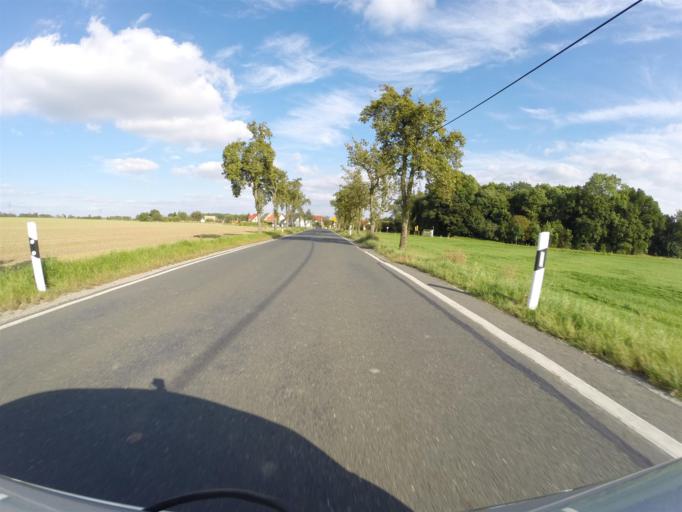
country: DE
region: Thuringia
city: Lehesten
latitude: 50.9599
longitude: 11.5676
